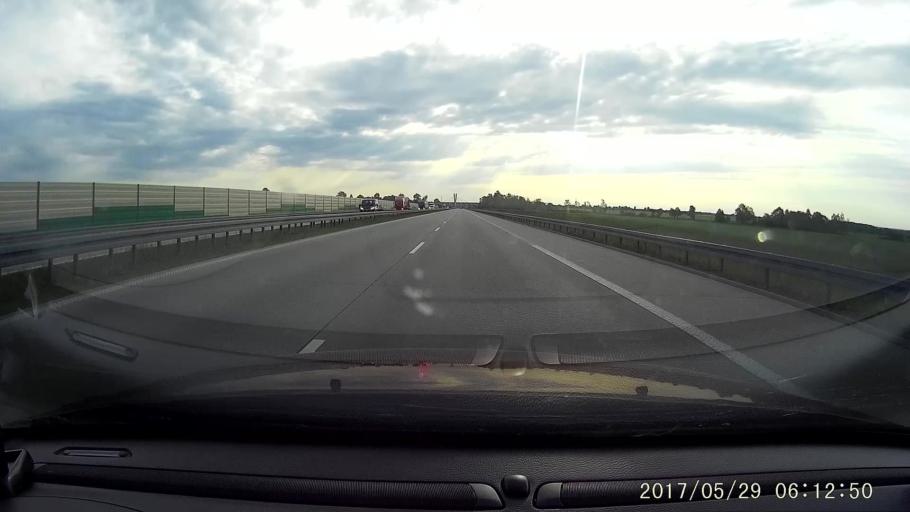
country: PL
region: Lower Silesian Voivodeship
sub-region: Powiat zgorzelecki
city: Wegliniec
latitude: 51.2220
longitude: 15.2855
